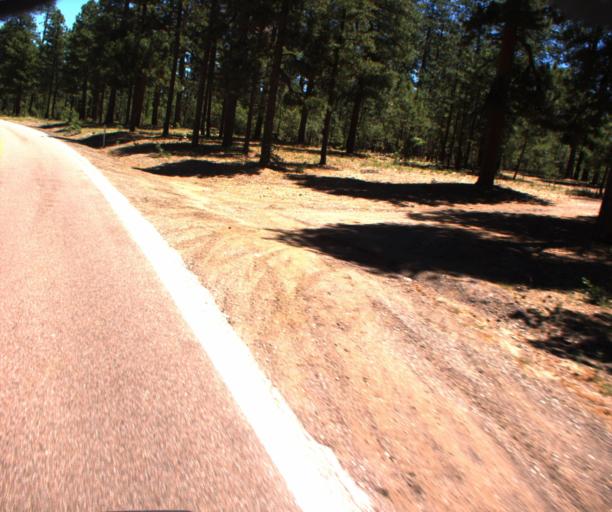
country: US
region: Arizona
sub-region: Gila County
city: Pine
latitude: 34.4415
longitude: -111.4551
